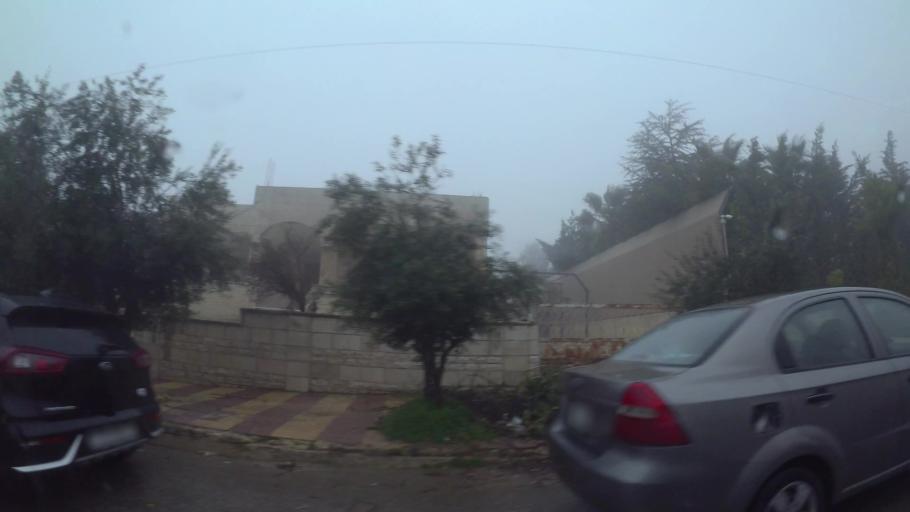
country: JO
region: Amman
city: Al Jubayhah
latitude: 32.0058
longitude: 35.8887
